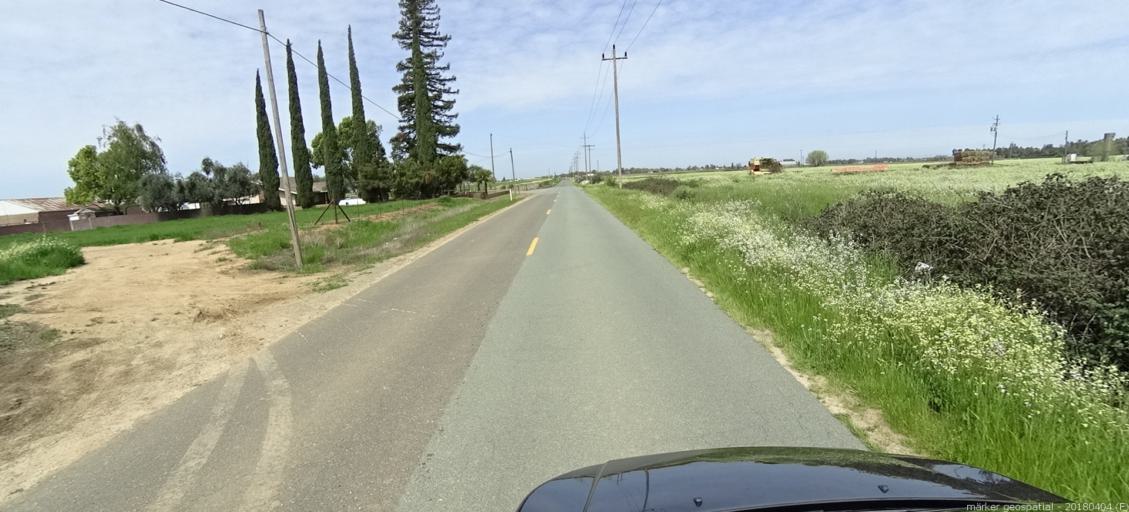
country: US
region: California
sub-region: Sacramento County
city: Herald
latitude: 38.2689
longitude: -121.2641
